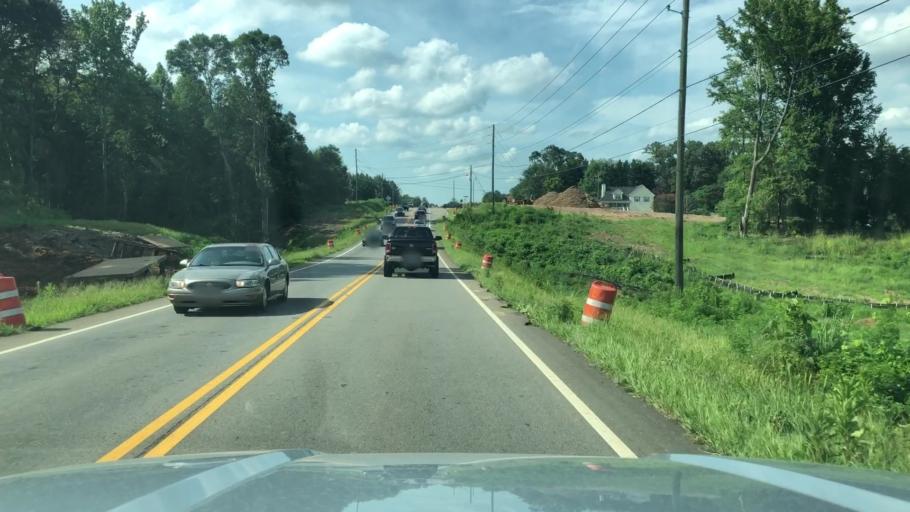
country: US
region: Georgia
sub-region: Paulding County
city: Hiram
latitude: 33.8223
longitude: -84.7588
